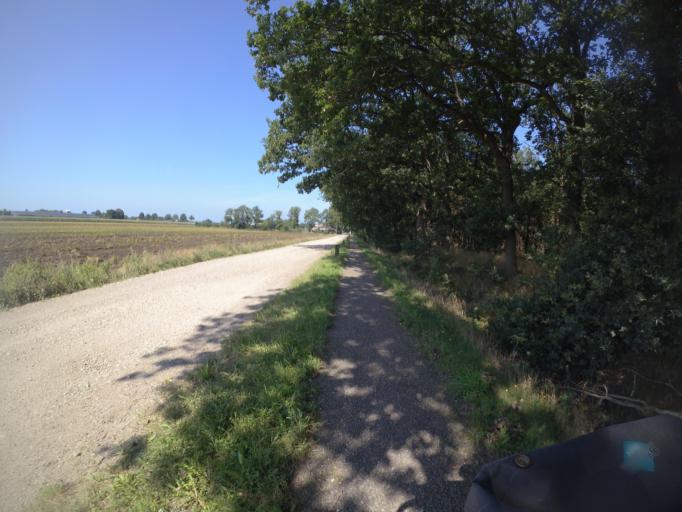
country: NL
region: North Brabant
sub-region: Gemeente Mill en Sint Hubert
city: Wilbertoord
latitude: 51.5809
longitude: 5.7988
